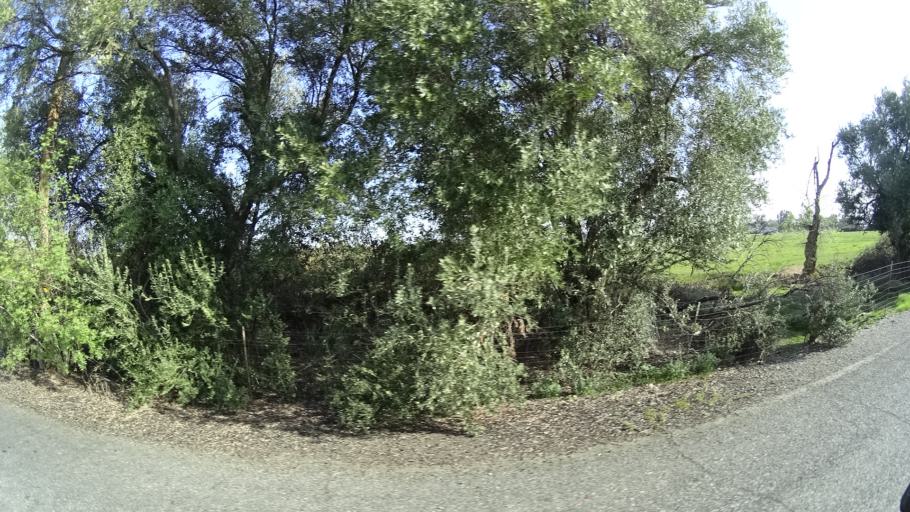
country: US
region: California
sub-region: Glenn County
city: Orland
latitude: 39.7187
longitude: -122.2198
